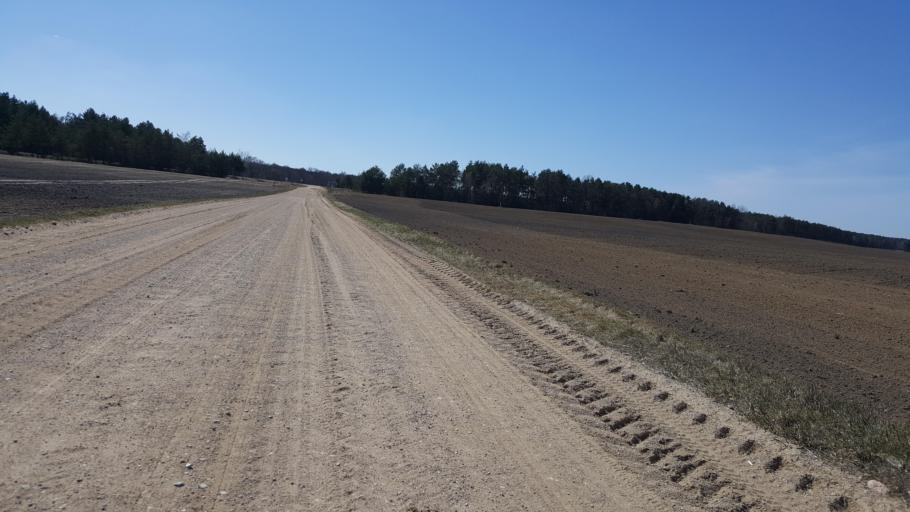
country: BY
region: Brest
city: Kamyanyets
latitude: 52.3091
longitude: 23.8590
